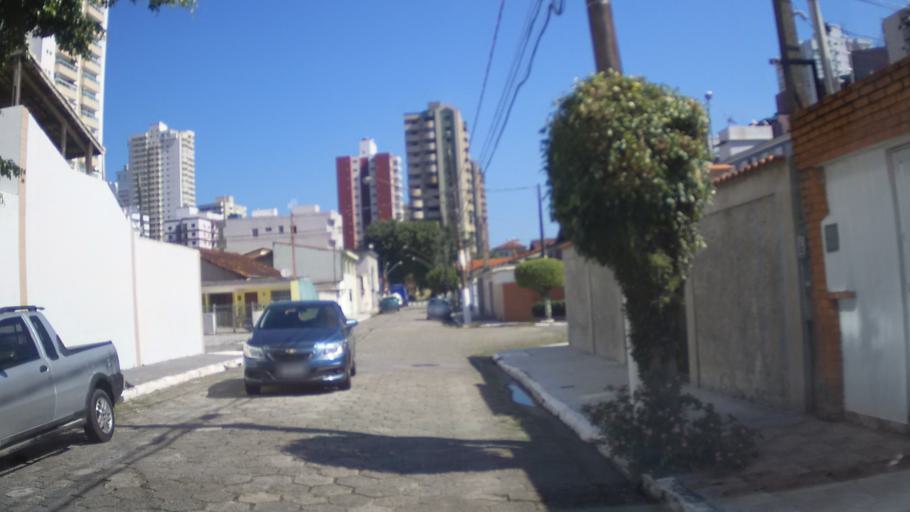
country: BR
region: Sao Paulo
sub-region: Praia Grande
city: Praia Grande
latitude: -24.0111
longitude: -46.4012
